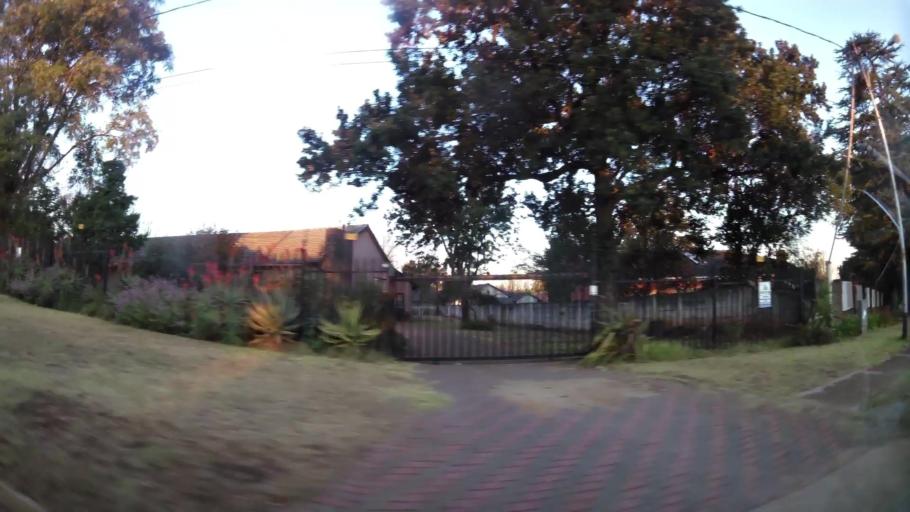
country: ZA
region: Gauteng
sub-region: City of Johannesburg Metropolitan Municipality
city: Roodepoort
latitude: -26.1550
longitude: 27.9083
